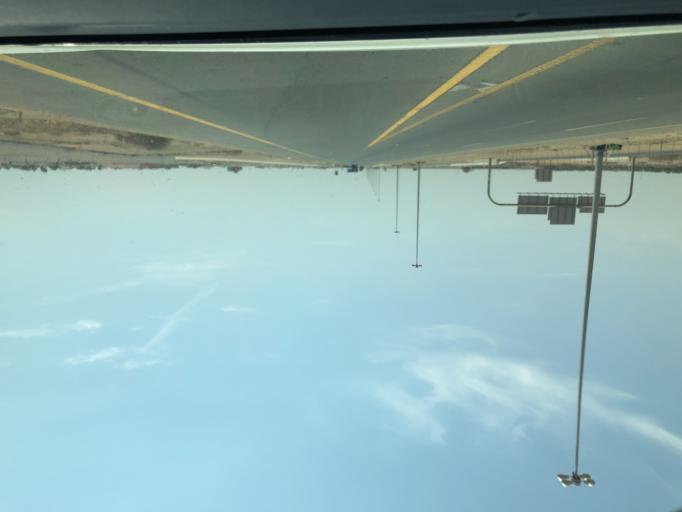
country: SA
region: Makkah
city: Rabigh
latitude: 22.2707
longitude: 39.1240
